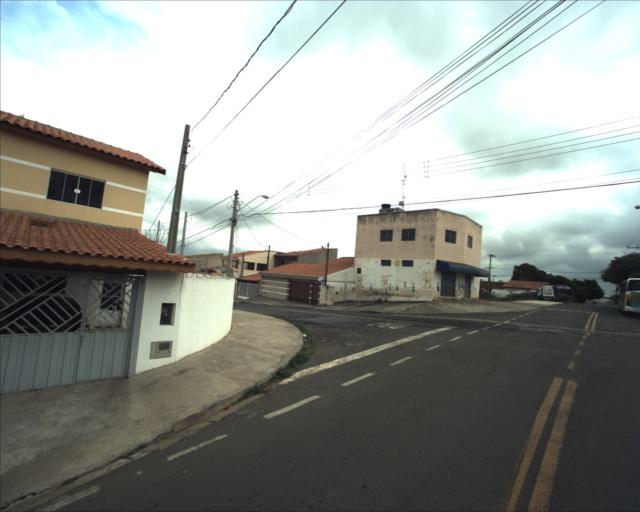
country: BR
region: Sao Paulo
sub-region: Sorocaba
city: Sorocaba
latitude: -23.4368
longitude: -47.5090
